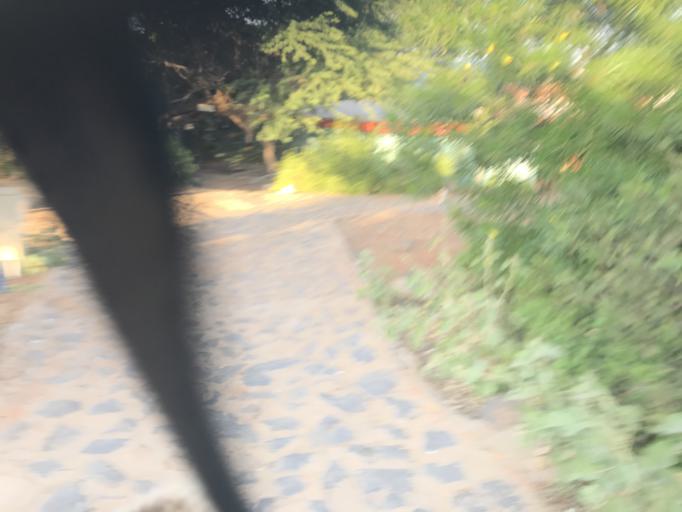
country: SN
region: Dakar
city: Dakar
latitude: 14.6653
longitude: -17.3980
